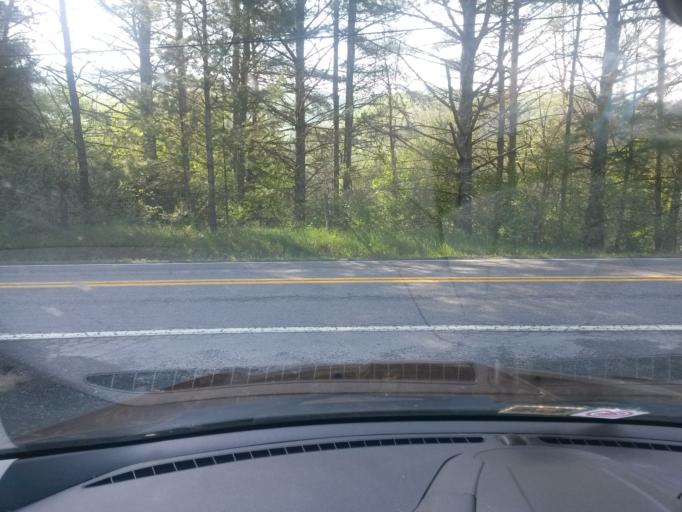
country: US
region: West Virginia
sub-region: Pocahontas County
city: Marlinton
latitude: 38.0348
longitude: -80.0345
